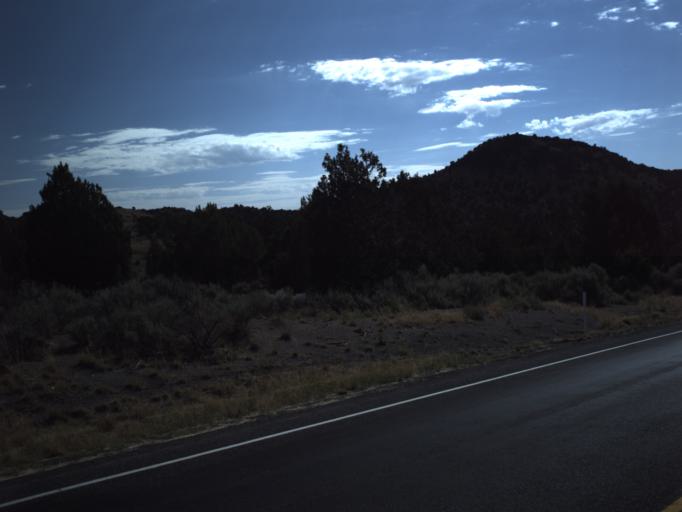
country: US
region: Utah
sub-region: Utah County
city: Genola
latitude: 39.9655
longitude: -112.0483
